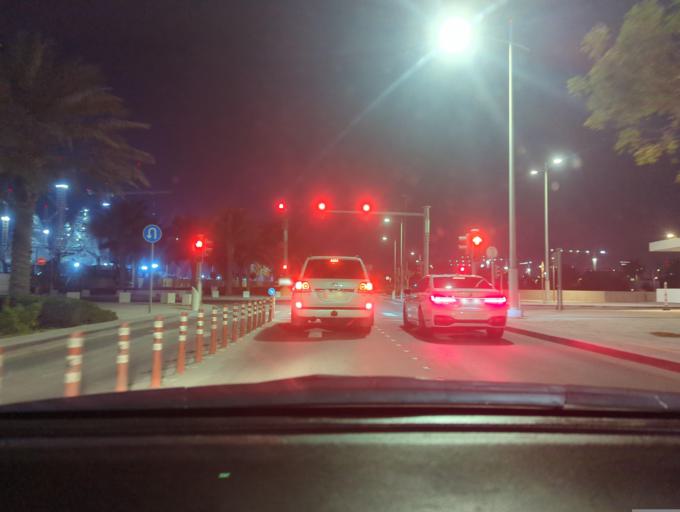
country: AE
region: Abu Dhabi
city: Abu Dhabi
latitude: 24.5361
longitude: 54.4001
